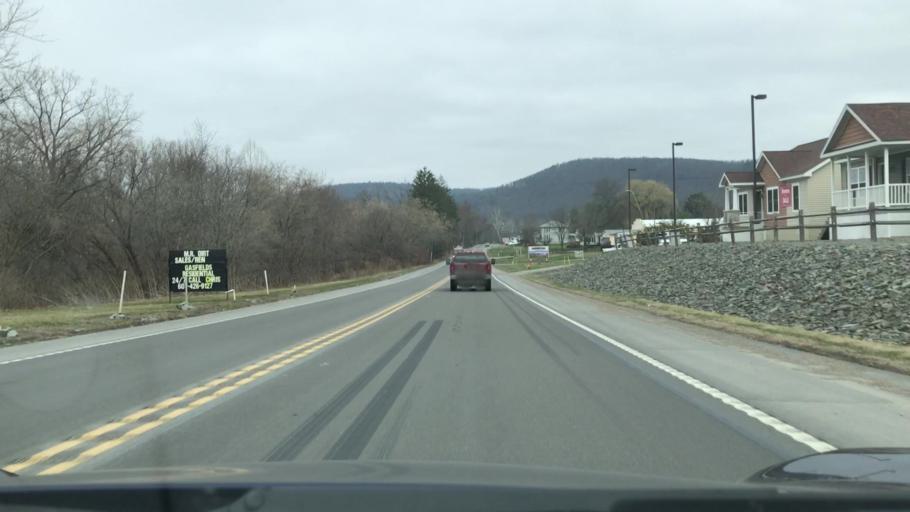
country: US
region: Pennsylvania
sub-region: Bradford County
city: Towanda
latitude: 41.7747
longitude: -76.3748
